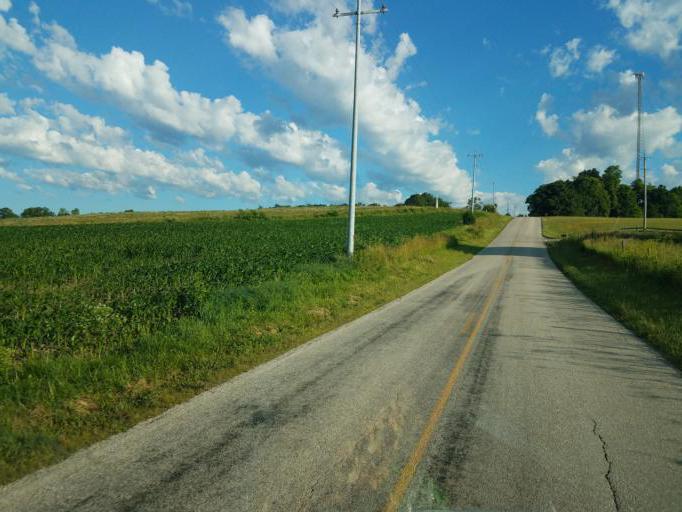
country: US
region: Ohio
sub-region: Sandusky County
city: Bellville
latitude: 40.5917
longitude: -82.3704
